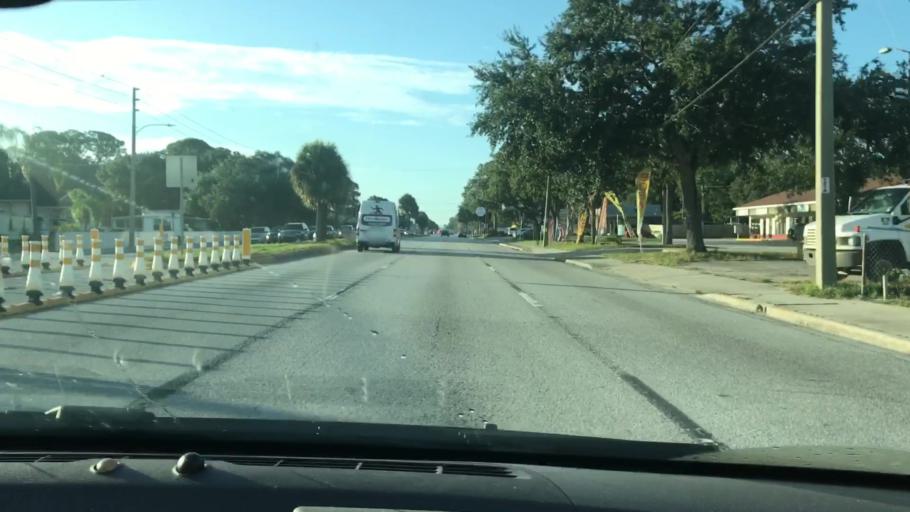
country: US
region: Florida
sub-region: Pinellas County
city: Pinellas Park
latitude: 27.8557
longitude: -82.7003
